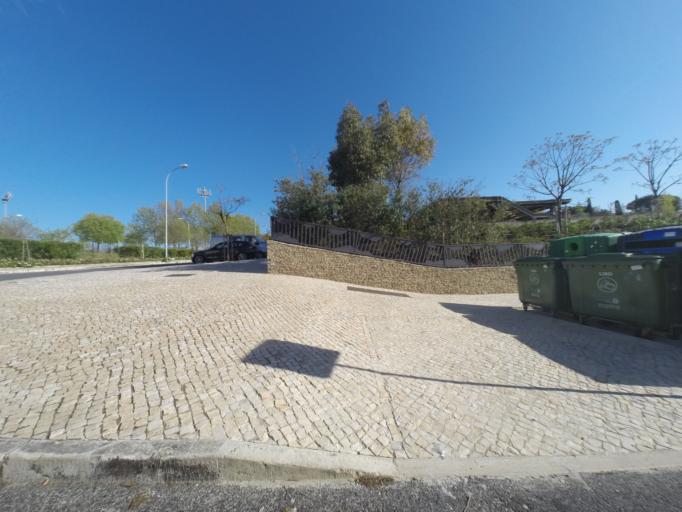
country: PT
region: Lisbon
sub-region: Oeiras
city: Oeiras
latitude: 38.6992
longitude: -9.3027
